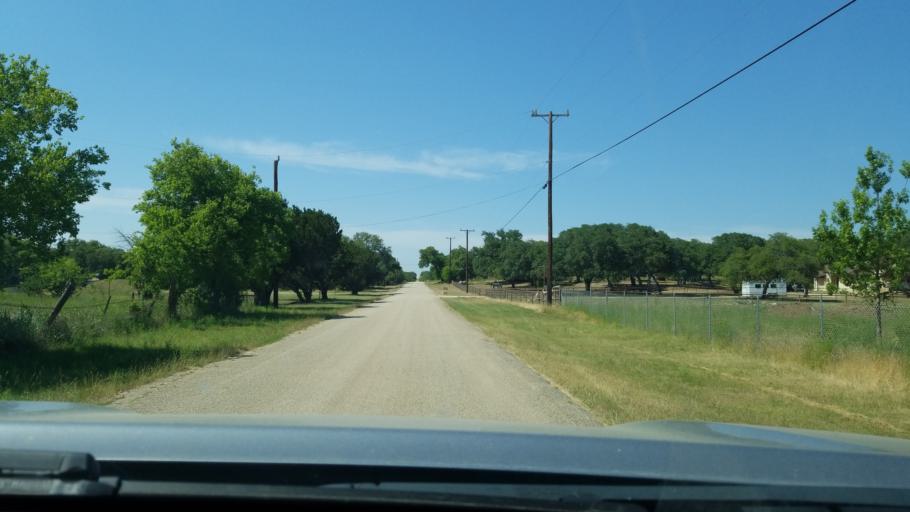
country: US
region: Texas
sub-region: Bexar County
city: Timberwood Park
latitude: 29.7528
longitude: -98.5153
